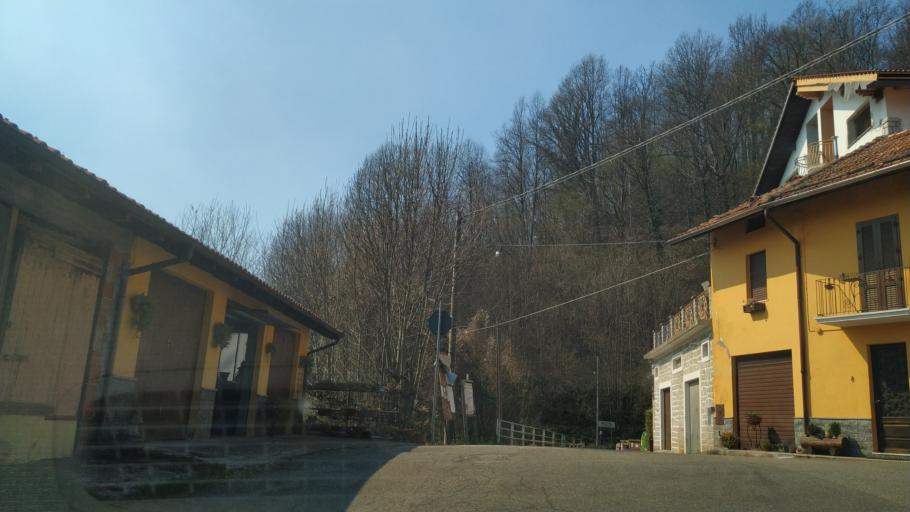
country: IT
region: Piedmont
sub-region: Provincia di Biella
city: Pray
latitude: 45.6855
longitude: 8.1997
